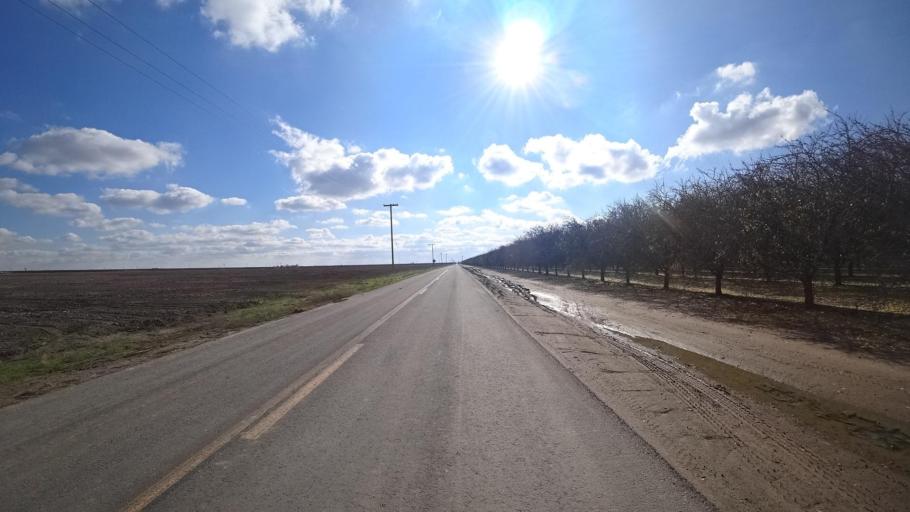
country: US
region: California
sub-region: Kern County
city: Wasco
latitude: 35.7174
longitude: -119.3660
